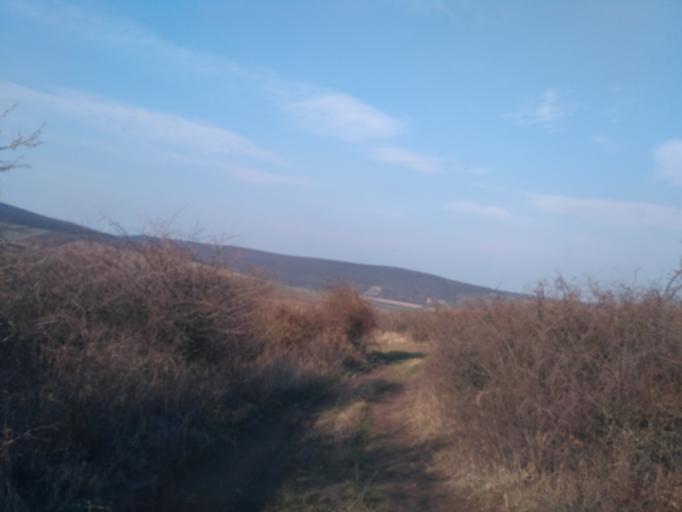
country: HU
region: Borsod-Abauj-Zemplen
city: Satoraljaujhely
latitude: 48.4309
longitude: 21.7096
